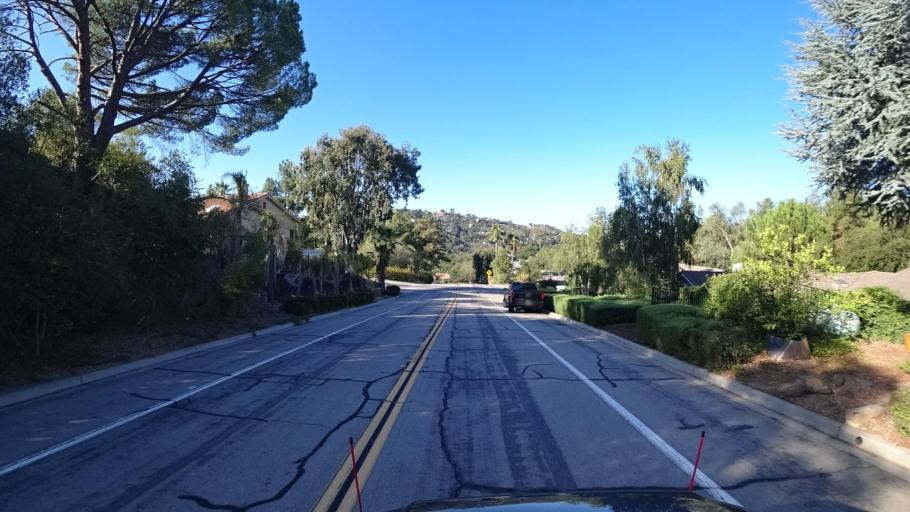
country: US
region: California
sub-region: San Diego County
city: Hidden Meadows
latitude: 33.2180
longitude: -117.1129
